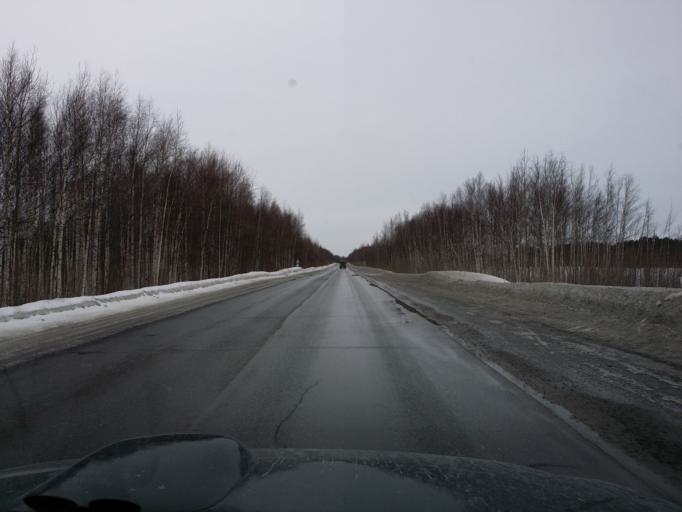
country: RU
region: Tomsk
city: Strezhevoy
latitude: 60.7422
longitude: 77.5307
